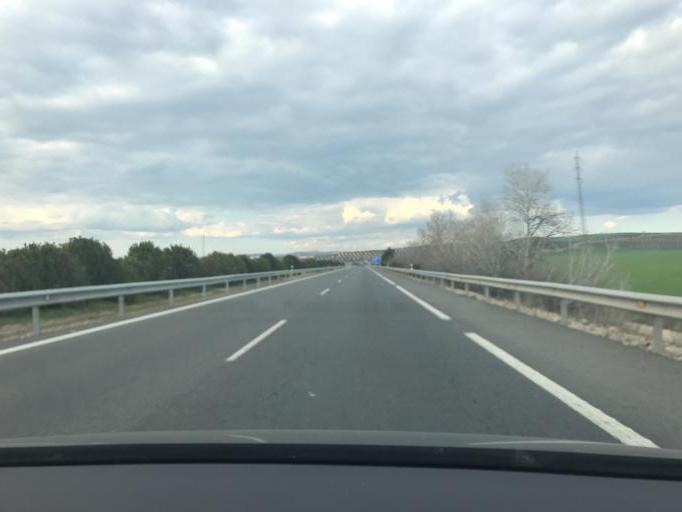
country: ES
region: Andalusia
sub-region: Province of Cordoba
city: Pedro Abad
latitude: 37.9862
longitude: -4.4385
